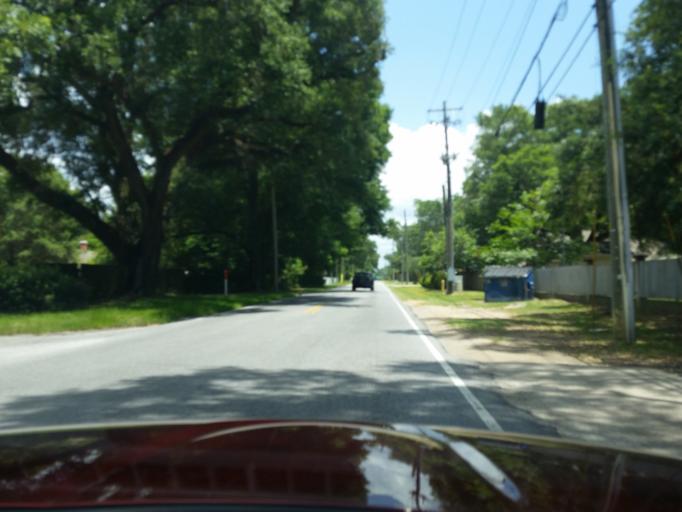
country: US
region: Florida
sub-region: Escambia County
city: Ensley
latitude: 30.5479
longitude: -87.2770
